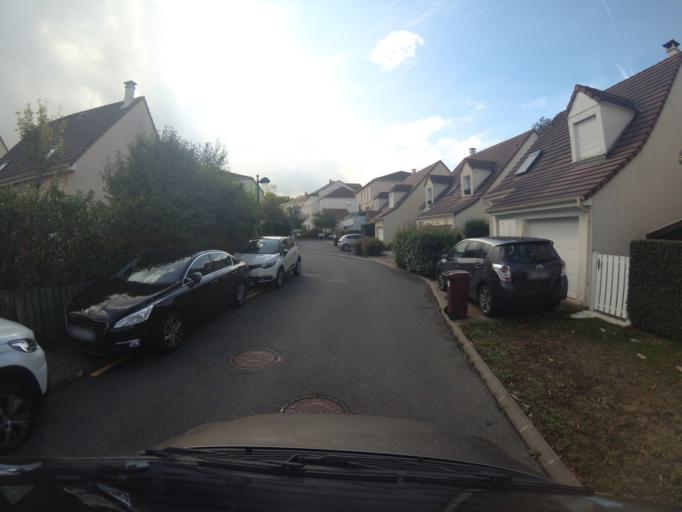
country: FR
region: Ile-de-France
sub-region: Departement de Seine-et-Marne
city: Montevrain
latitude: 48.8700
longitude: 2.7531
